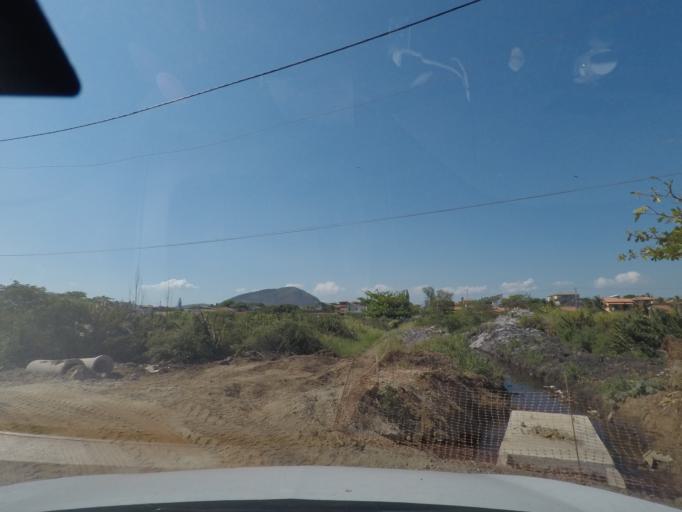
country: BR
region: Rio de Janeiro
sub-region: Marica
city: Marica
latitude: -22.9702
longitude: -42.9478
